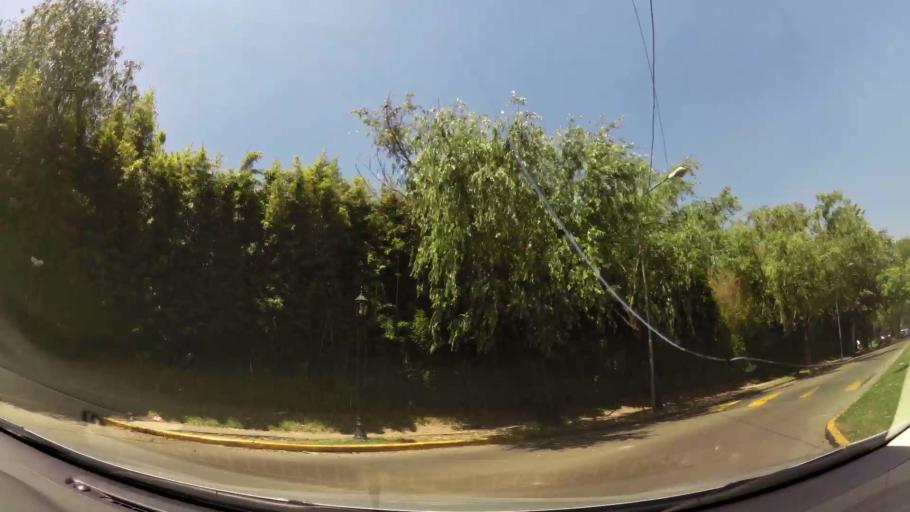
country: AR
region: Buenos Aires
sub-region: Partido de Tigre
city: Tigre
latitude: -34.4288
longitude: -58.5951
